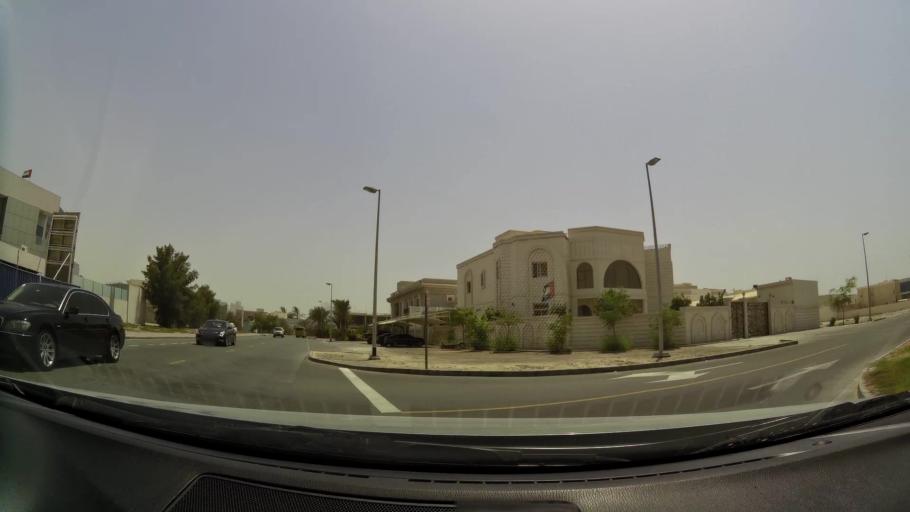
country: AE
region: Dubai
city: Dubai
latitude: 25.1298
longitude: 55.2036
